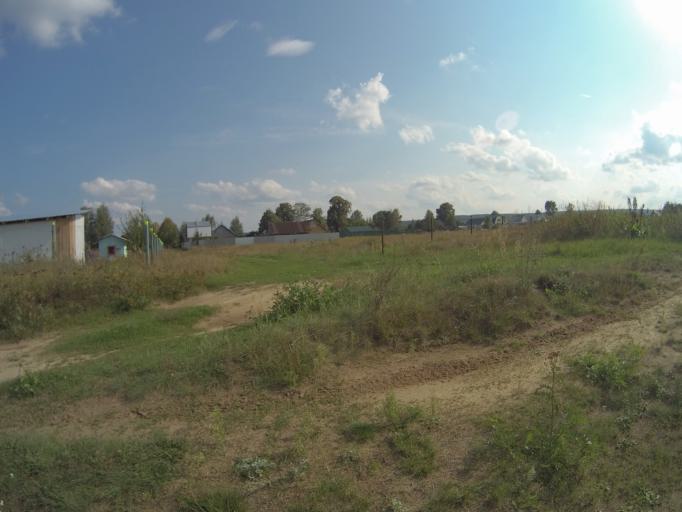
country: RU
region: Vladimir
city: Raduzhnyy
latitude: 56.0378
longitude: 40.3017
